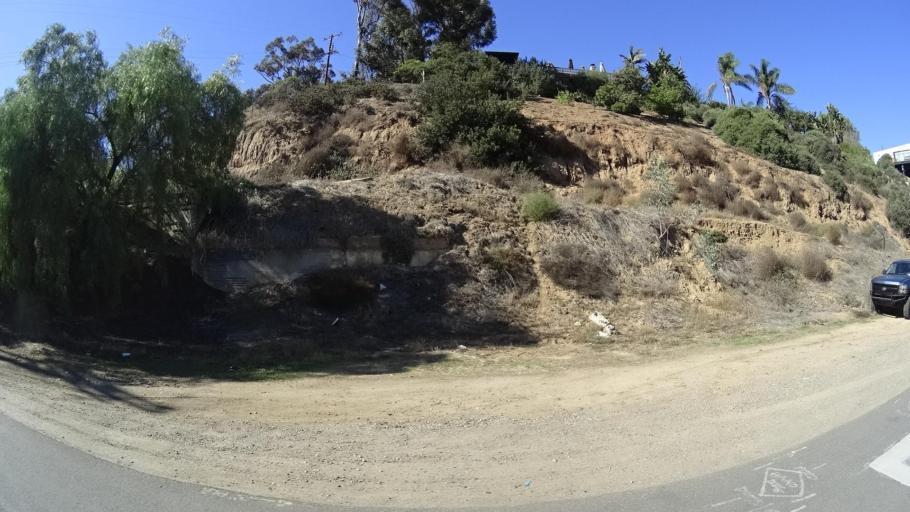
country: US
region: California
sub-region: San Diego County
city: Bonita
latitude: 32.6758
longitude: -117.0233
